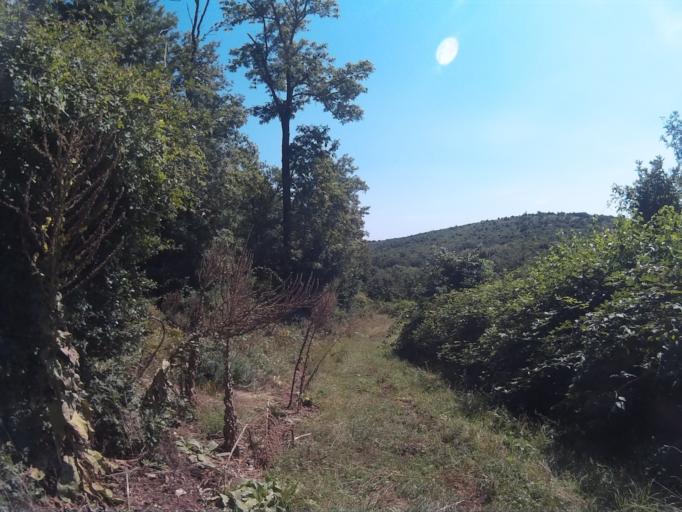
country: HU
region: Veszprem
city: Zirc
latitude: 47.1776
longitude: 17.8709
